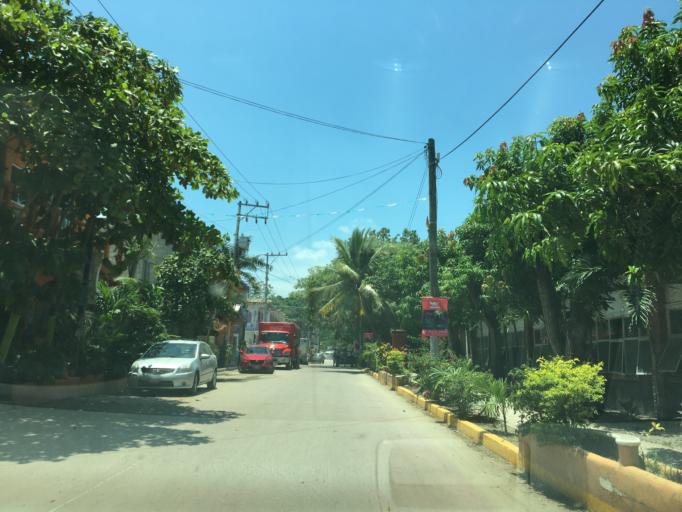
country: MX
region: Nayarit
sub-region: Bahia de Banderas
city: Lo de Marcos
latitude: 20.8959
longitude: -105.4089
